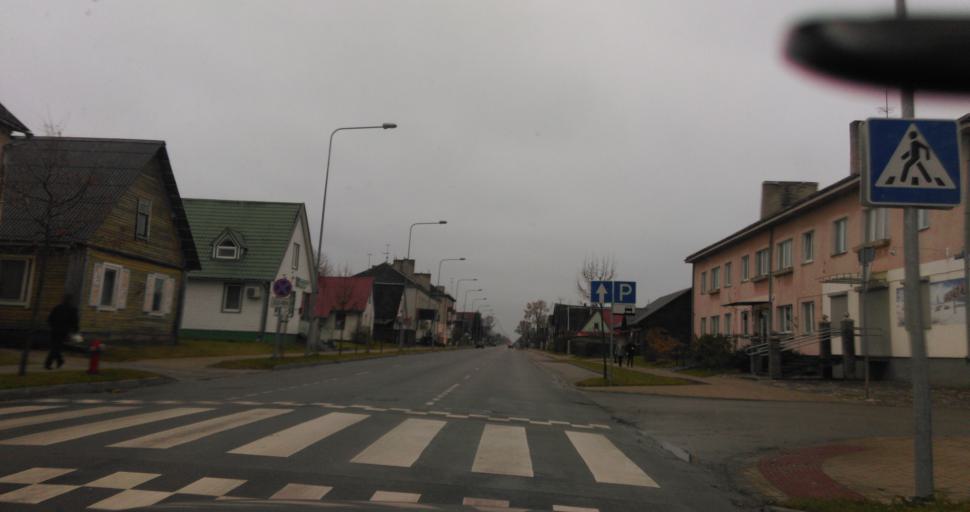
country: LT
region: Panevezys
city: Rokiskis
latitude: 55.9629
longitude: 25.5866
